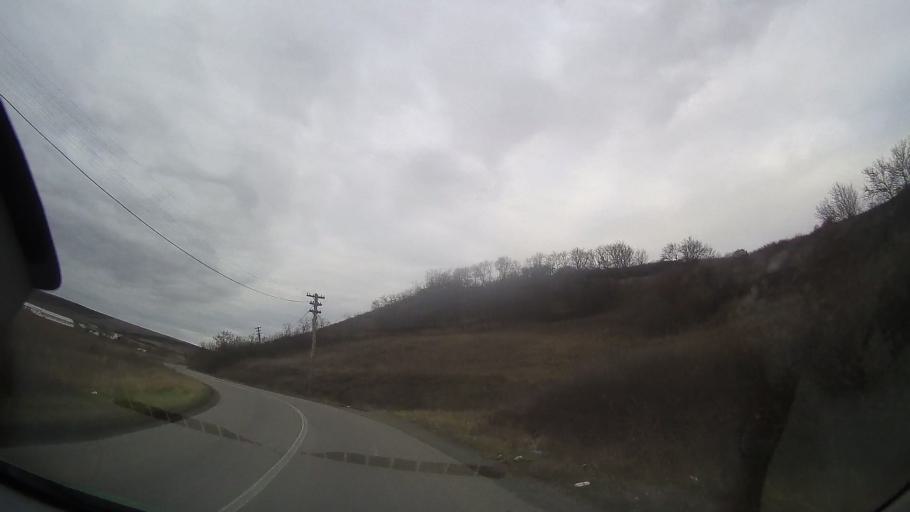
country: RO
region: Mures
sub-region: Comuna Faragau
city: Faragau
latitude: 46.7537
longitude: 24.5221
